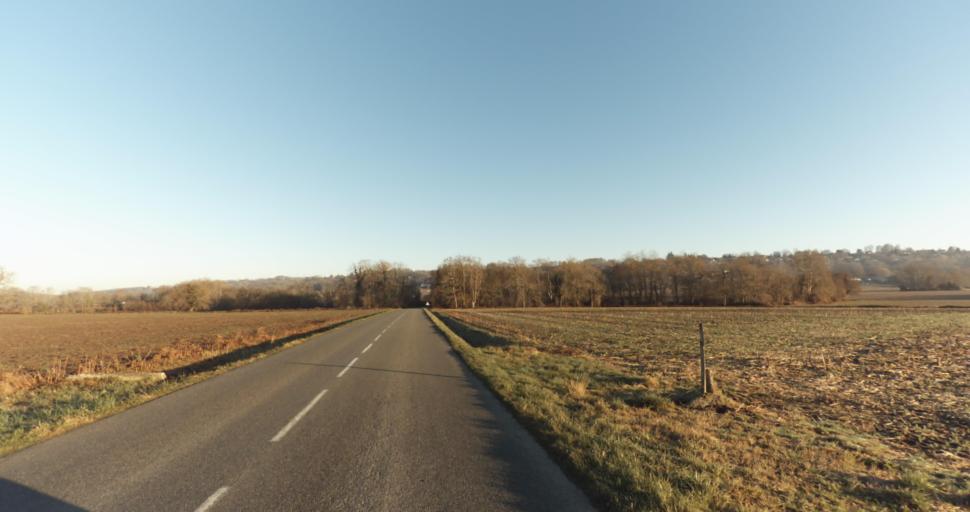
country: FR
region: Aquitaine
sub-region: Departement des Pyrenees-Atlantiques
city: Morlaas
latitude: 43.3182
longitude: -0.2749
